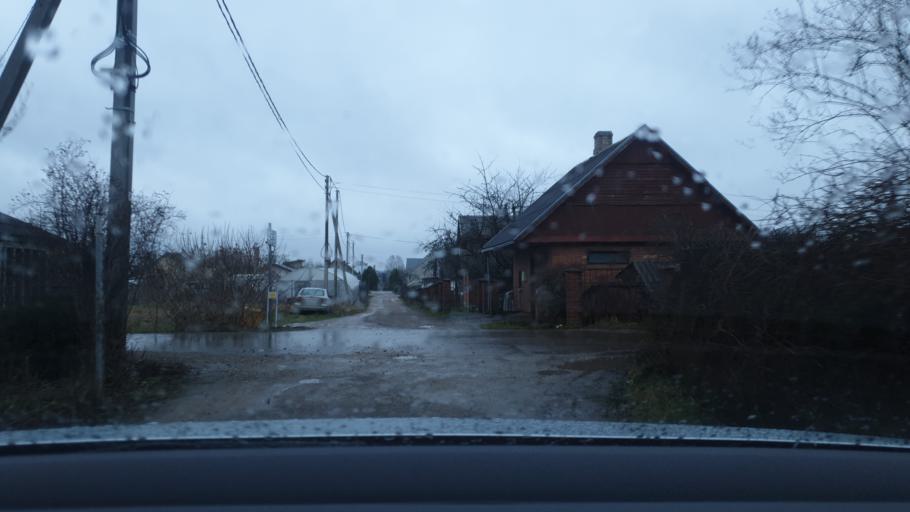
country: LT
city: Skaidiskes
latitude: 54.7057
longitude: 25.4043
